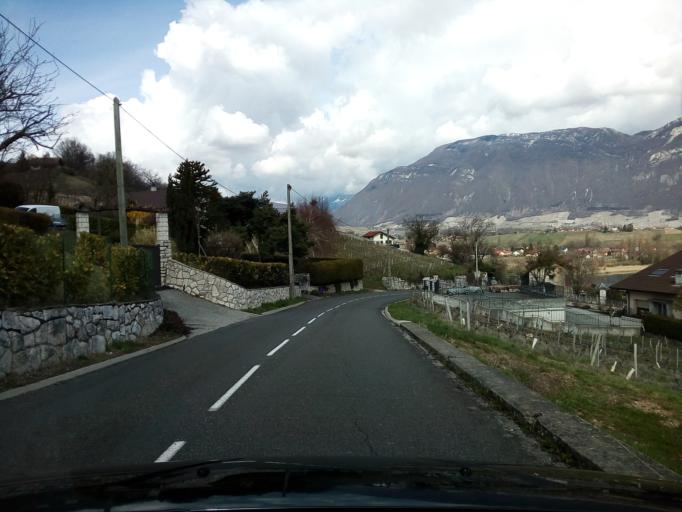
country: FR
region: Rhone-Alpes
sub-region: Departement de la Savoie
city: Les Marches
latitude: 45.4918
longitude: 5.9814
